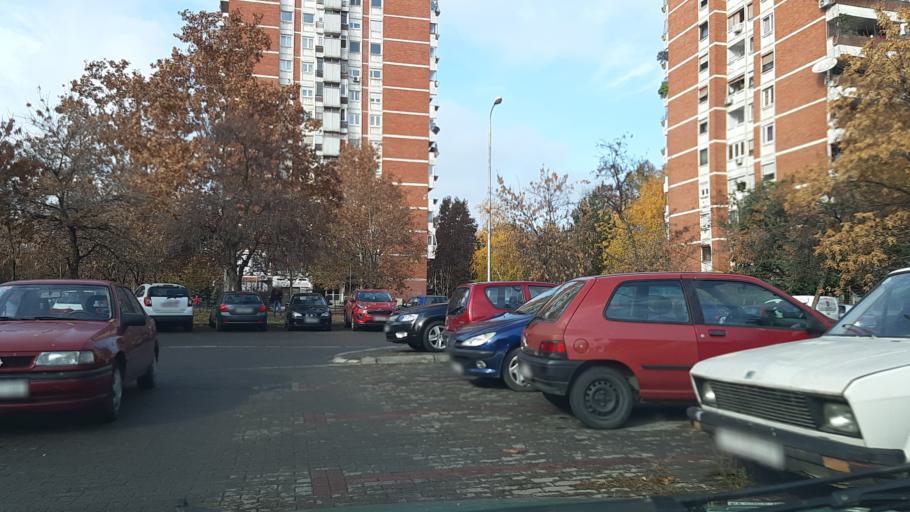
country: MK
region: Kisela Voda
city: Usje
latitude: 41.9885
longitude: 21.4689
